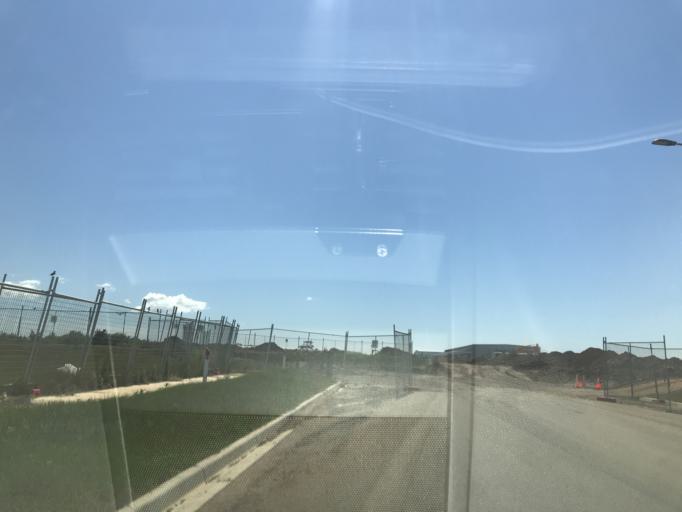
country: AU
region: Victoria
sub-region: Wyndham
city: Truganina
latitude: -37.8336
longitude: 144.7361
